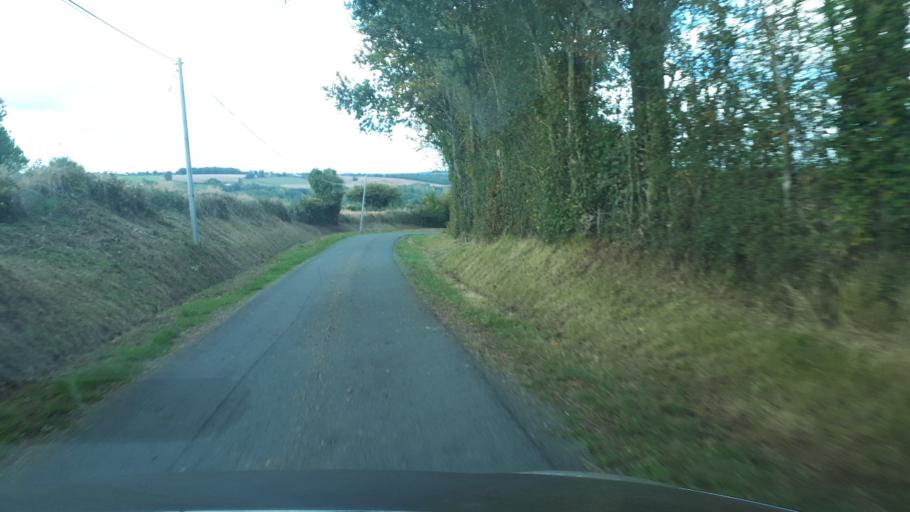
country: FR
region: Centre
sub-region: Departement du Loir-et-Cher
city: Sarge-sur-Braye
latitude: 47.9137
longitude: 0.8595
